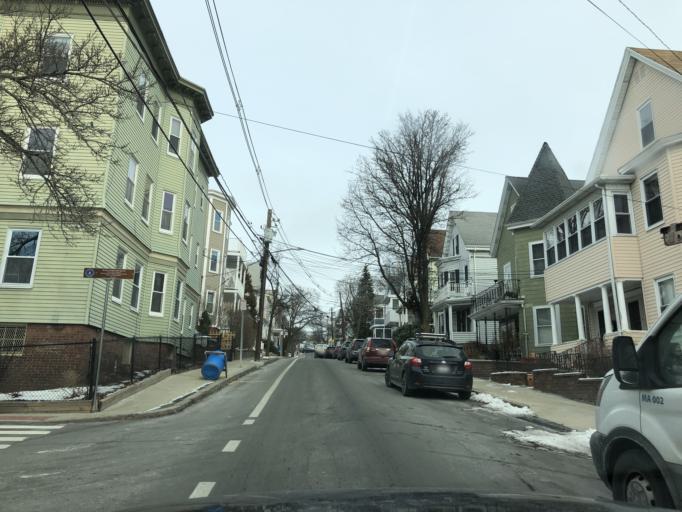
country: US
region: Massachusetts
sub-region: Middlesex County
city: Somerville
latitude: 42.3862
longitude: -71.1108
